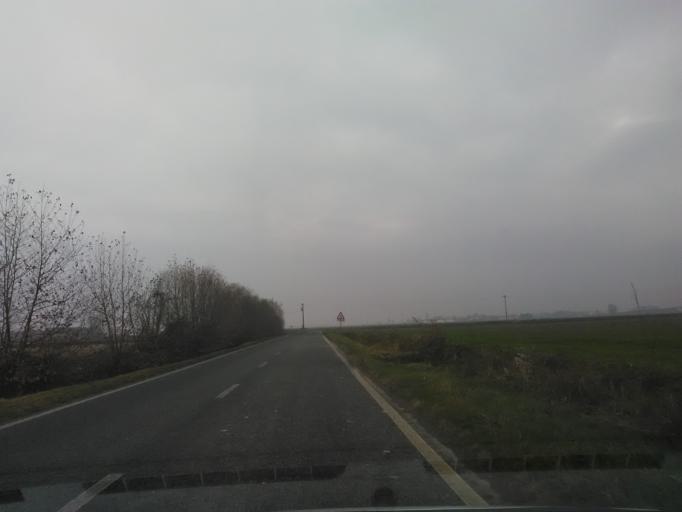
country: IT
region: Piedmont
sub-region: Provincia di Vercelli
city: Salasco
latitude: 45.3151
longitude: 8.2400
